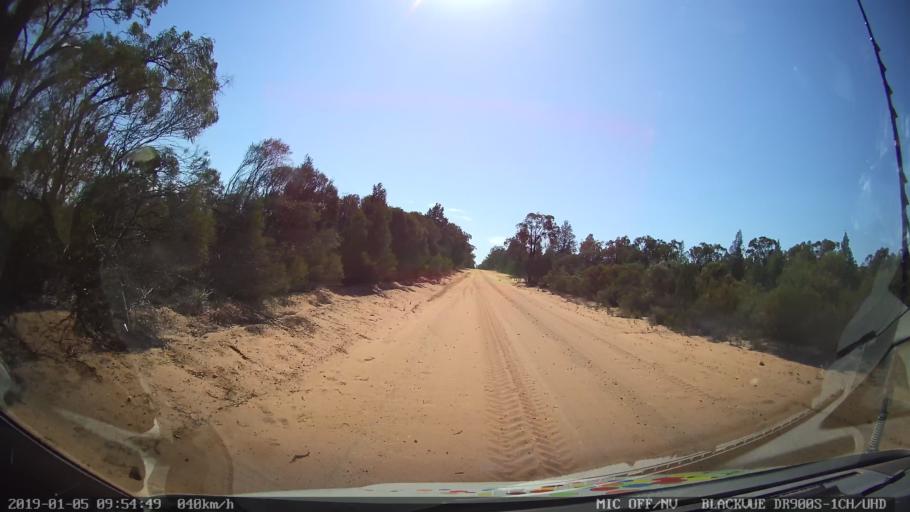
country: AU
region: New South Wales
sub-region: Gilgandra
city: Gilgandra
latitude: -31.6634
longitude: 148.7827
